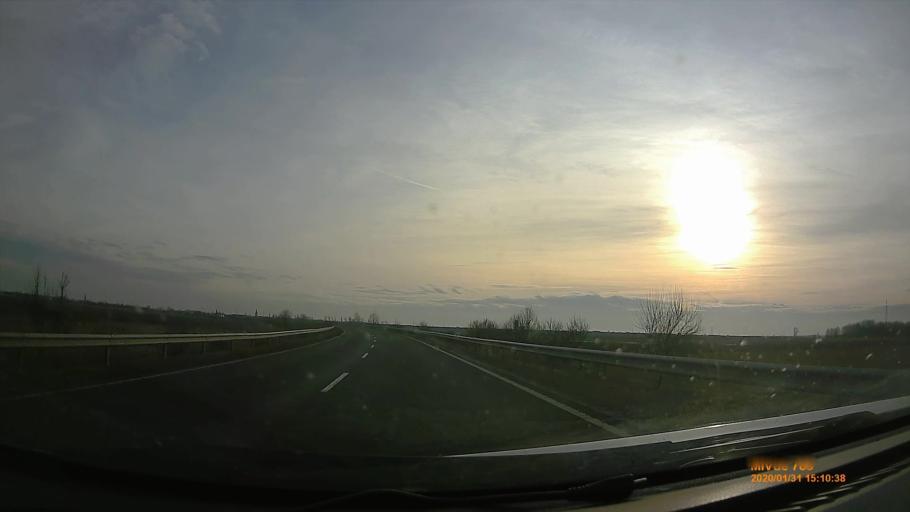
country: HU
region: Hajdu-Bihar
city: Polgar
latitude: 47.8595
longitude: 21.1508
